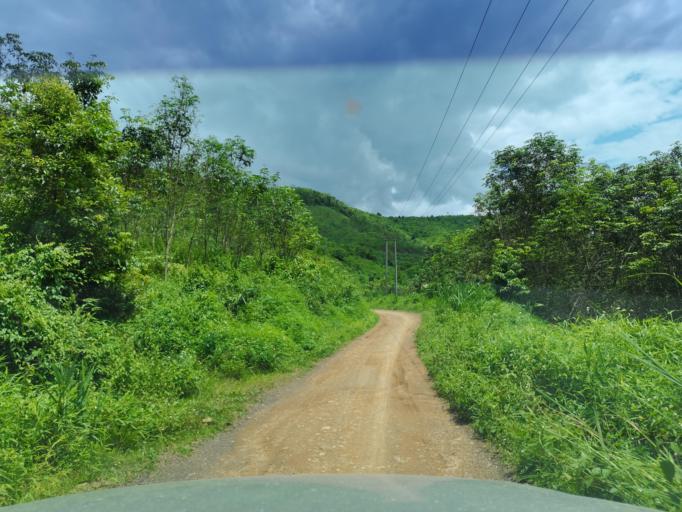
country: LA
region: Loungnamtha
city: Muang Long
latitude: 20.7175
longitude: 101.0145
